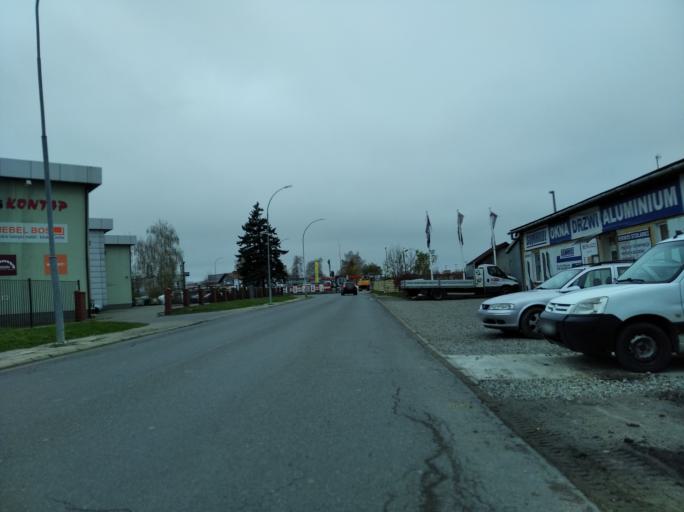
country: PL
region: Subcarpathian Voivodeship
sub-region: Krosno
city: Krosno
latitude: 49.6930
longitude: 21.7501
